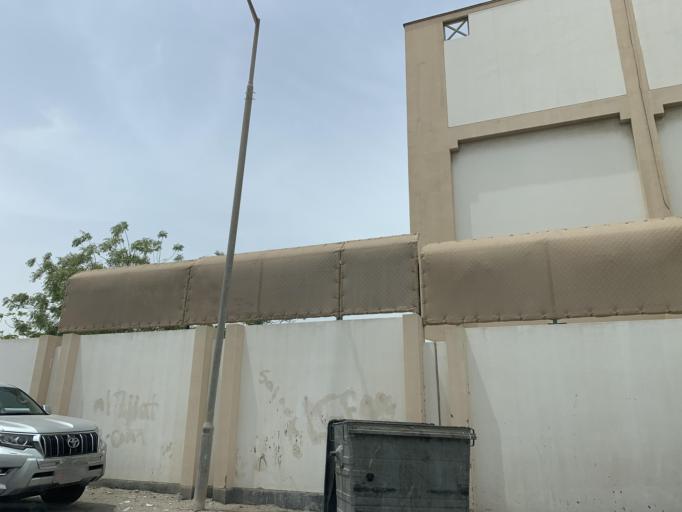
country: BH
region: Northern
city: Ar Rifa'
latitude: 26.1351
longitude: 50.5647
